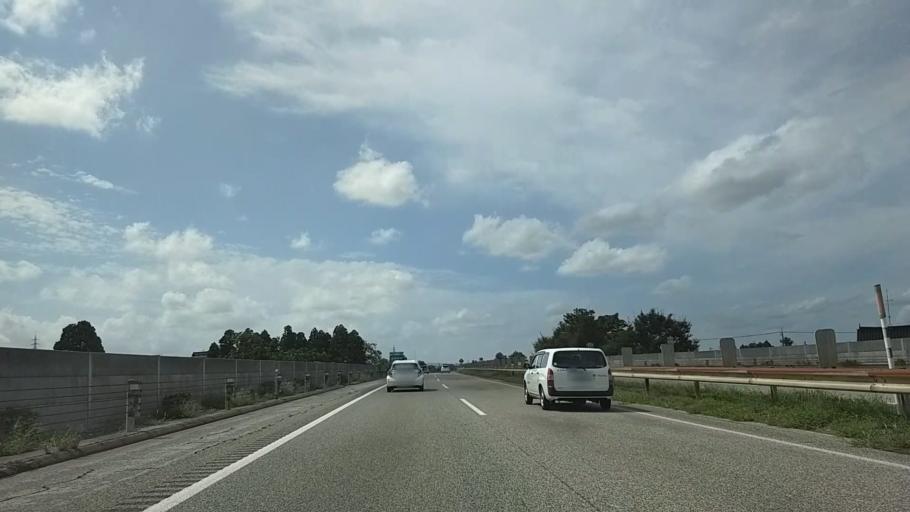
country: JP
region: Toyama
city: Takaoka
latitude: 36.6614
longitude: 137.0196
